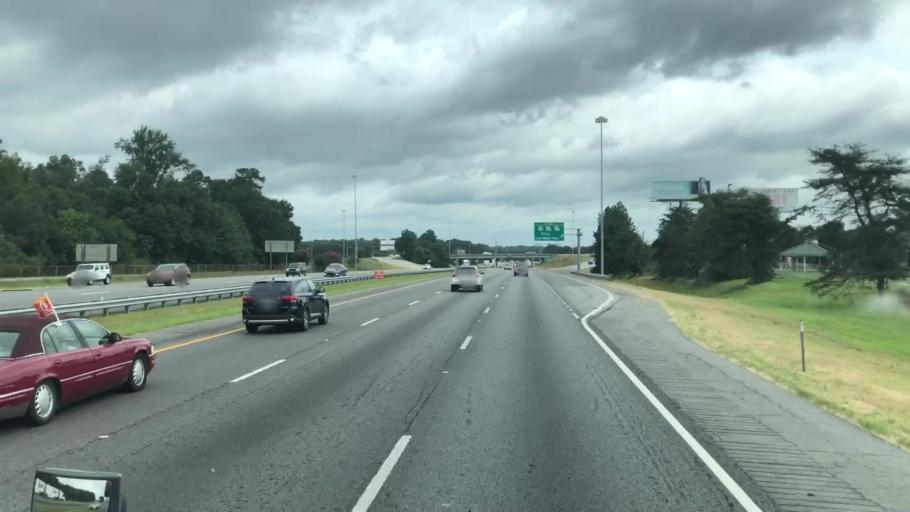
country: US
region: Georgia
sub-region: Houston County
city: Perry
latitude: 32.4423
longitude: -83.7551
